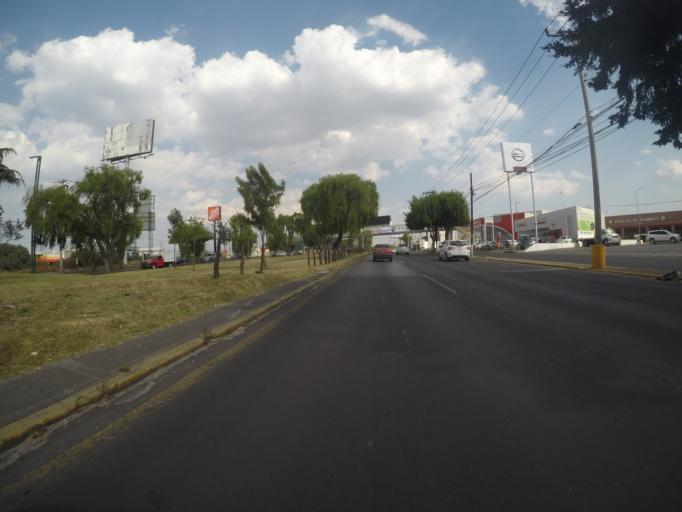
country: MX
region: Mexico
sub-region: Metepec
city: San Jorge Pueblo Nuevo
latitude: 19.2528
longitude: -99.6169
